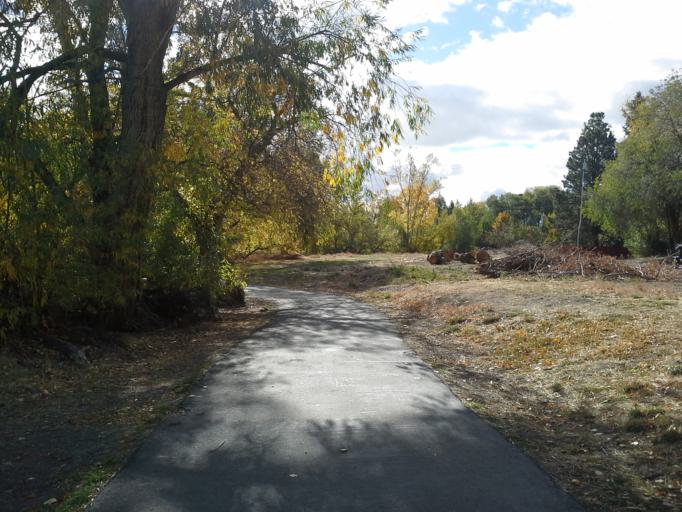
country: US
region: Oregon
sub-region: Baker County
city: Baker City
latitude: 44.7834
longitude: -117.8279
